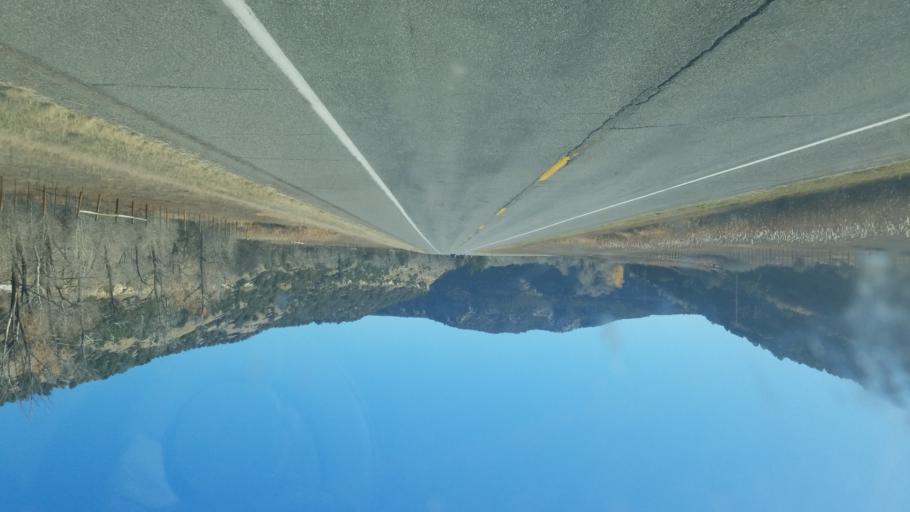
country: US
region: Colorado
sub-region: Ouray County
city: Ouray
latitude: 38.2419
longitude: -107.7451
